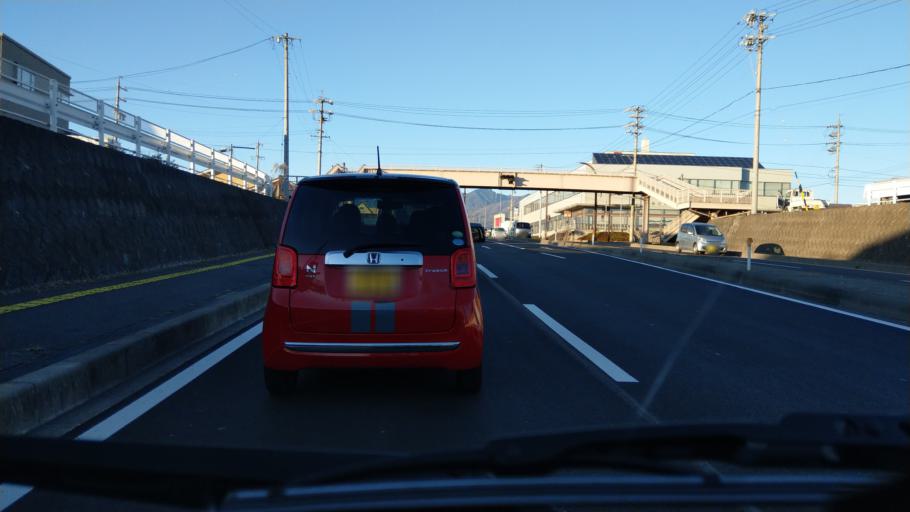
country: JP
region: Nagano
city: Saku
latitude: 36.2489
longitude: 138.4675
